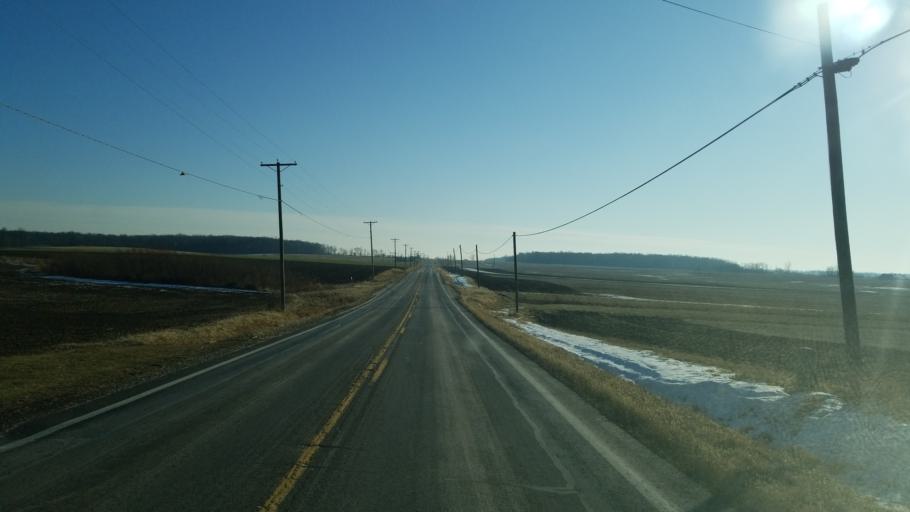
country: US
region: Ohio
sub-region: Sandusky County
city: Green Springs
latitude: 41.1026
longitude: -83.0155
